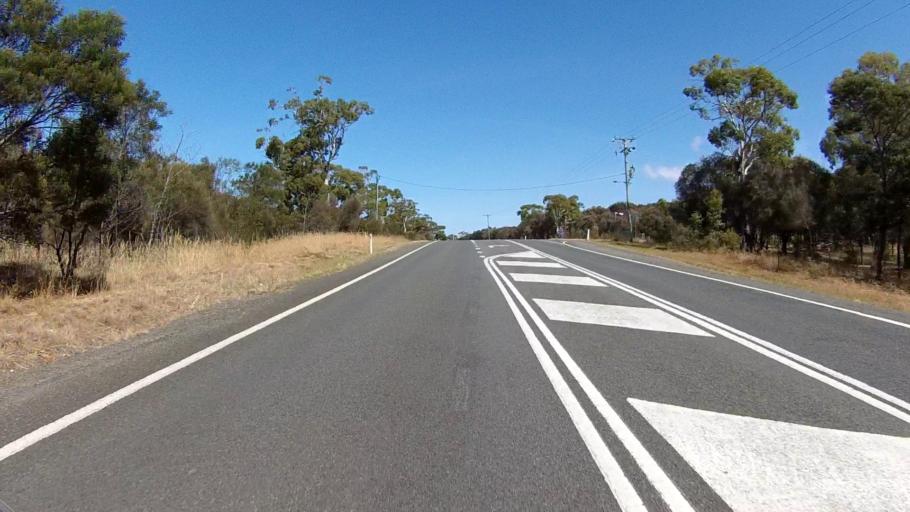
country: AU
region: Tasmania
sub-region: Sorell
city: Sorell
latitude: -42.1424
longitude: 148.0690
